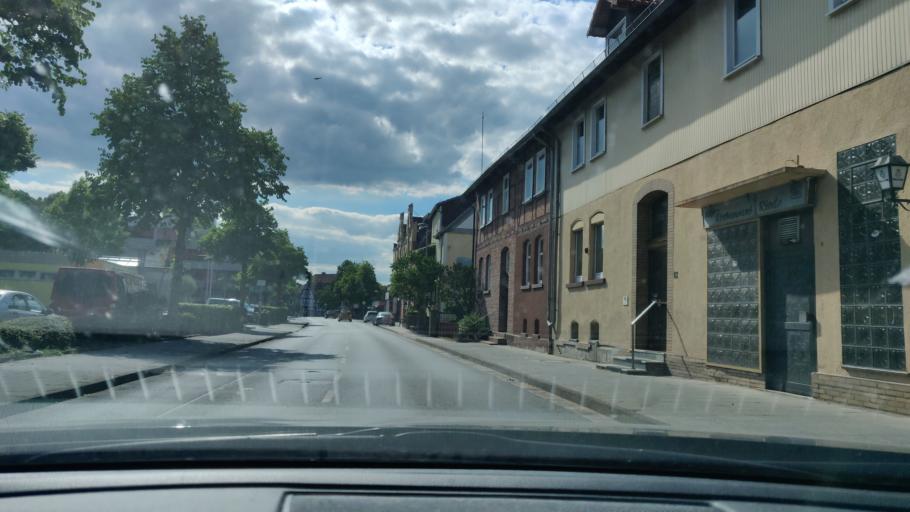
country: DE
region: Hesse
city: Gudensberg
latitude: 51.1784
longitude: 9.3692
